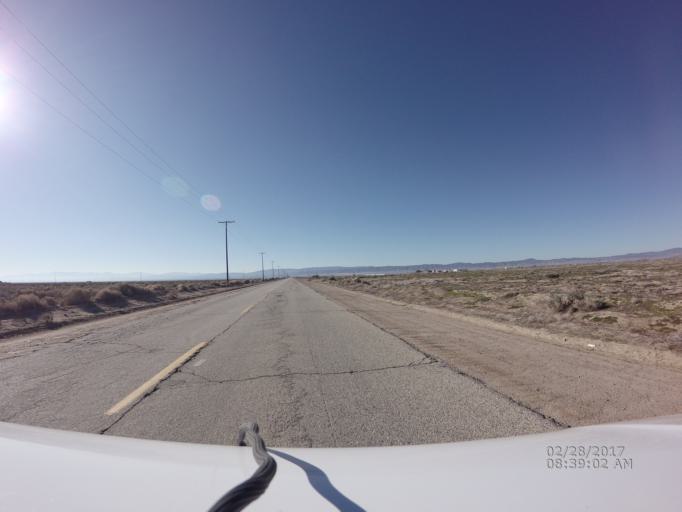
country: US
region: California
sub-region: Kern County
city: Rosamond
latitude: 34.7857
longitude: -118.2375
